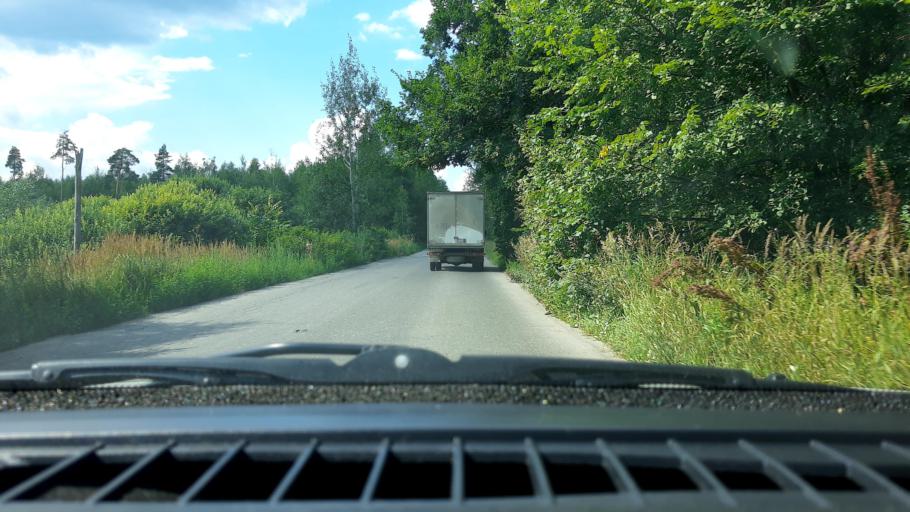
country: RU
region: Nizjnij Novgorod
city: Babino
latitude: 56.3139
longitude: 43.6268
